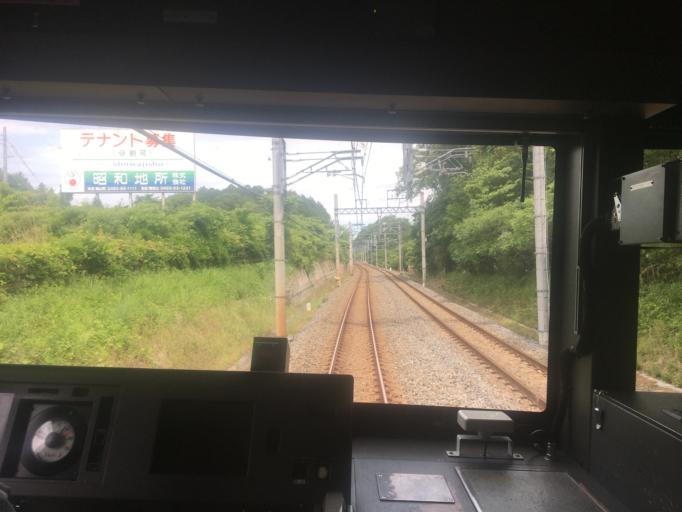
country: JP
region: Saitama
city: Ogawa
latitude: 36.0528
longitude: 139.3040
